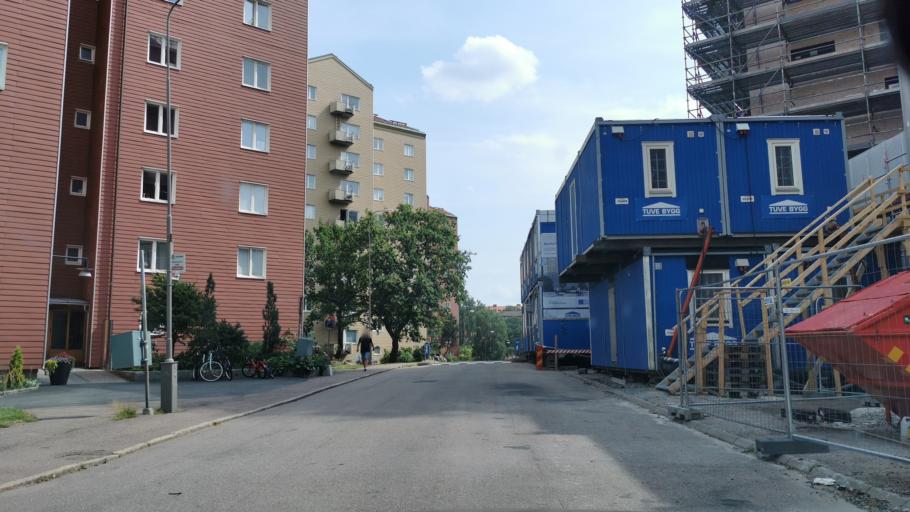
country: SE
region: Vaestra Goetaland
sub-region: Goteborg
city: Goeteborg
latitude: 57.6811
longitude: 11.9704
